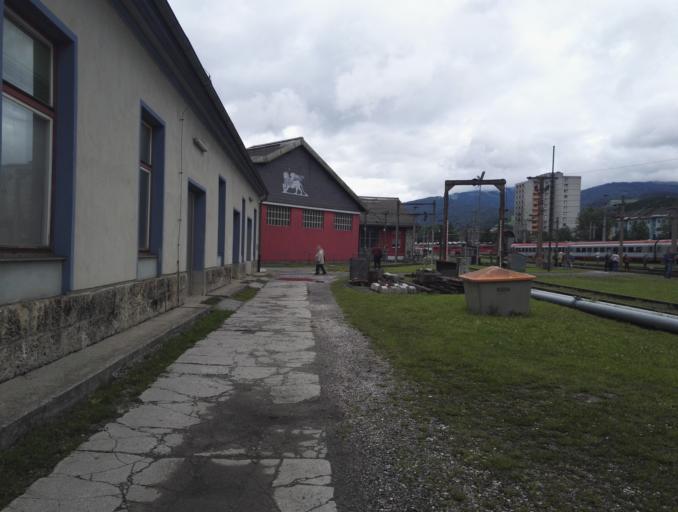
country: AT
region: Styria
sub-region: Politischer Bezirk Bruck-Muerzzuschlag
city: Muerzzuschlag
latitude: 47.6084
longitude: 15.6822
